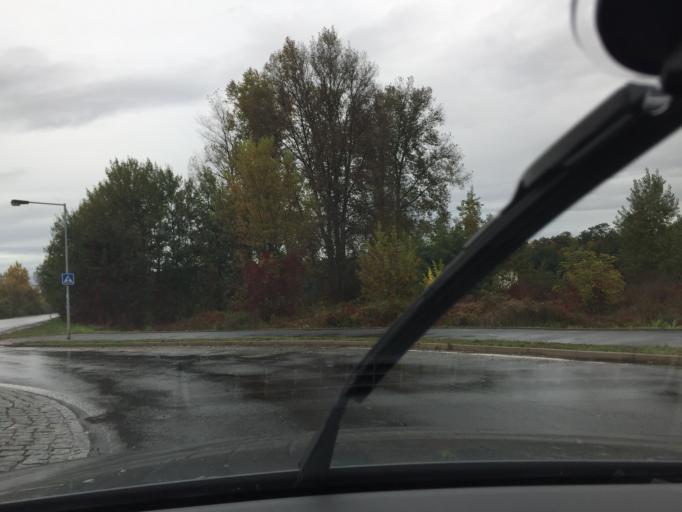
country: CZ
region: Central Bohemia
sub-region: Okres Melnik
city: Veltrusy
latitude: 50.2727
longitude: 14.3198
